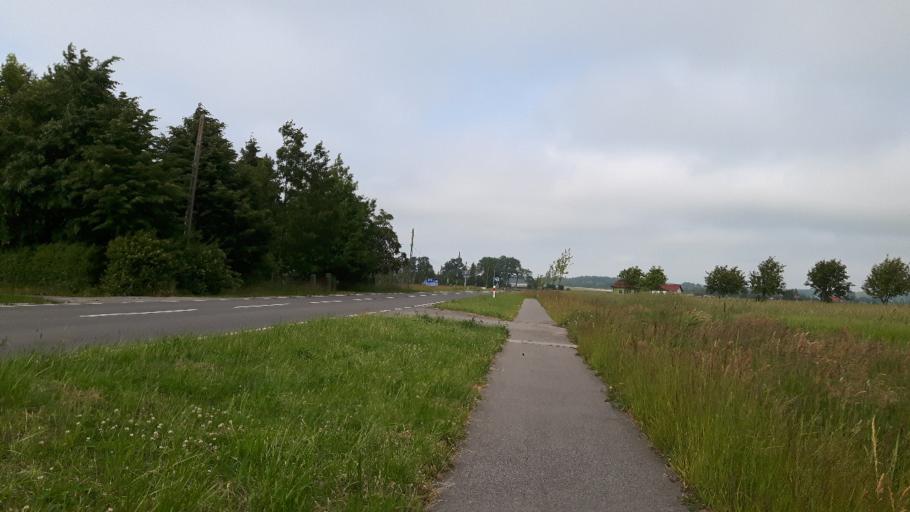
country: PL
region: West Pomeranian Voivodeship
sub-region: Powiat koszalinski
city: Sianow
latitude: 54.3367
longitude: 16.3169
